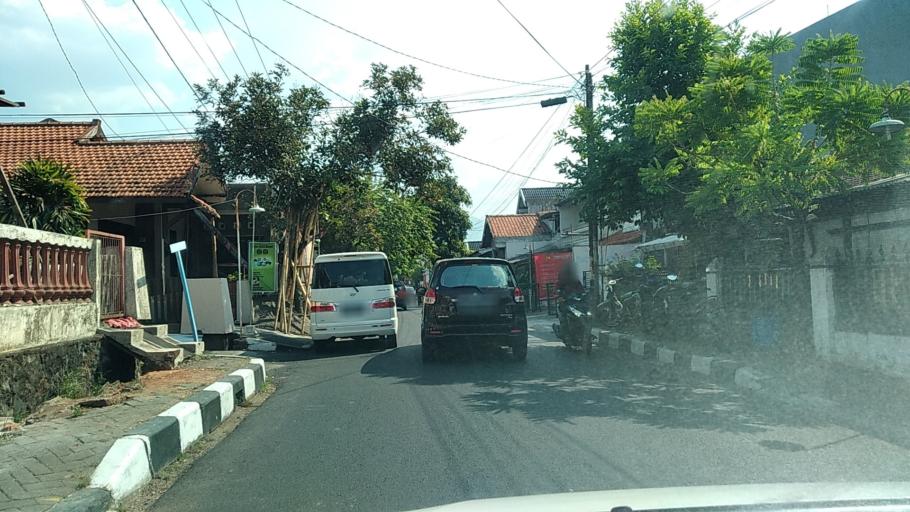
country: ID
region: Central Java
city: Ungaran
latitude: -7.0738
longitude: 110.4205
